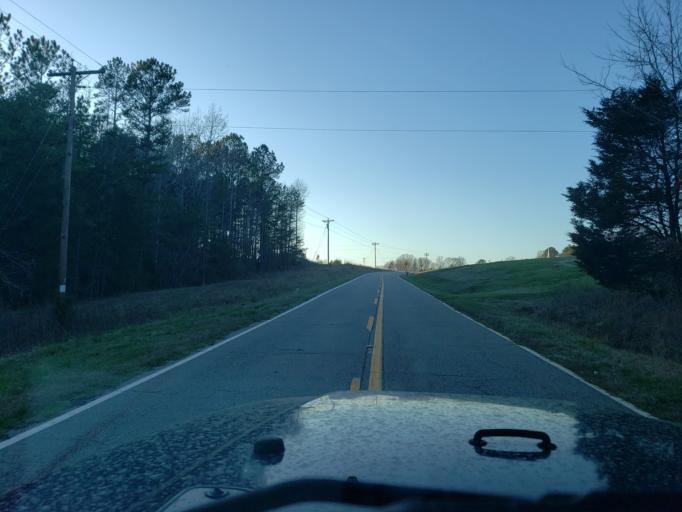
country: US
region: South Carolina
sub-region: Cherokee County
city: Blacksburg
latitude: 35.0505
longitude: -81.4204
